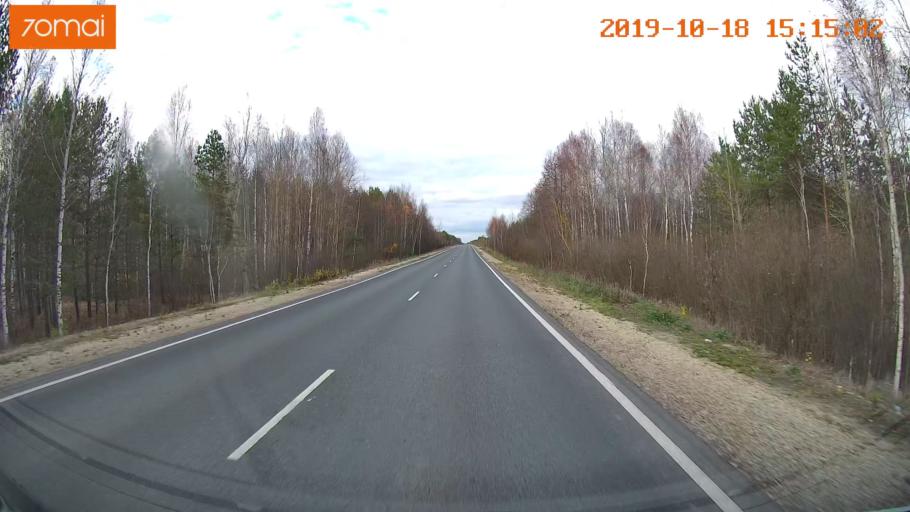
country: RU
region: Vladimir
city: Gus'-Khrustal'nyy
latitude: 55.6122
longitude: 40.7215
